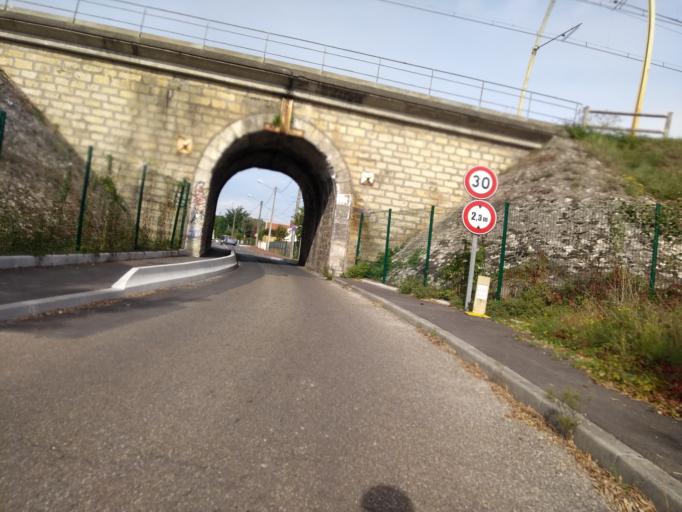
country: FR
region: Aquitaine
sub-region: Departement de la Gironde
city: Talence
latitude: 44.8095
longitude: -0.6178
